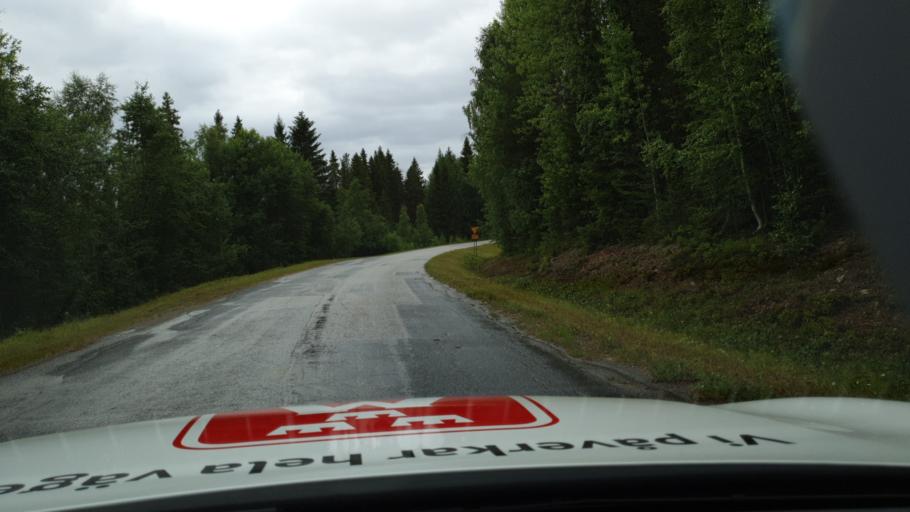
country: SE
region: Vaesterbotten
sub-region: Dorotea Kommun
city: Dorotea
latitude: 64.1269
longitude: 16.2287
